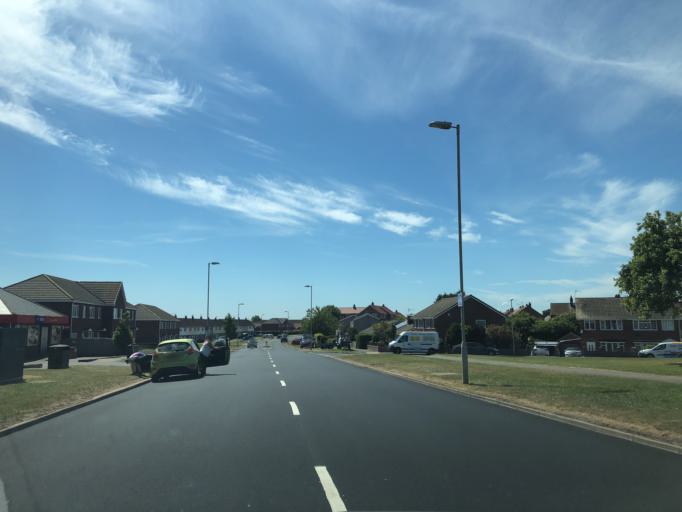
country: GB
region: England
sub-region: North Yorkshire
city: Scarborough
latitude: 54.2417
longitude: -0.3925
